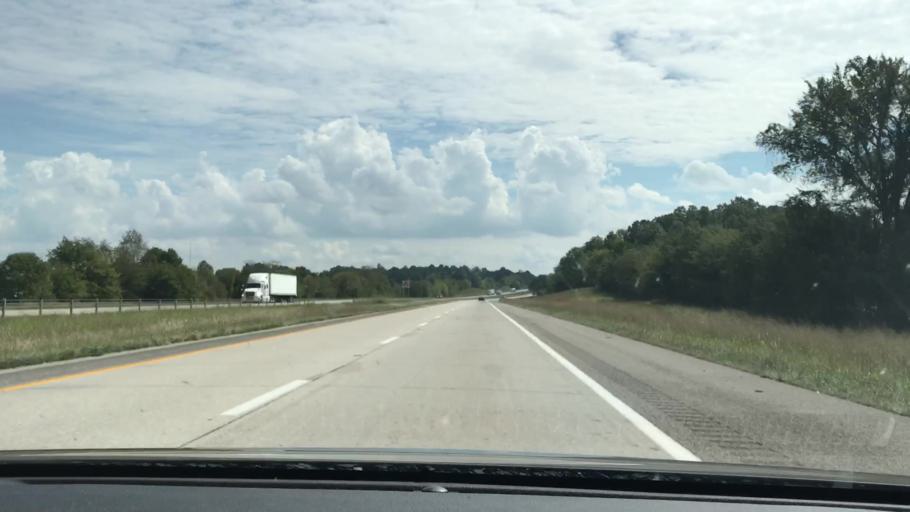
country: US
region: Kentucky
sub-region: Trigg County
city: Cadiz
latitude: 36.9090
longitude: -87.7782
